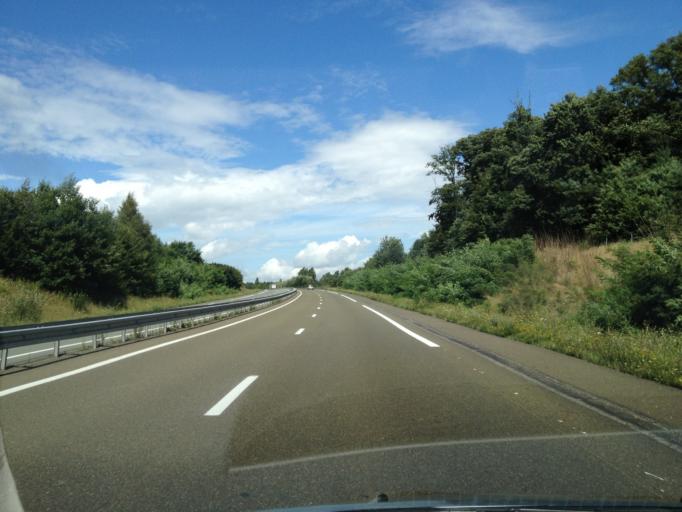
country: FR
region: Pays de la Loire
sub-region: Departement de la Sarthe
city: Neuville-sur-Sarthe
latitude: 48.0861
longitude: 0.1767
